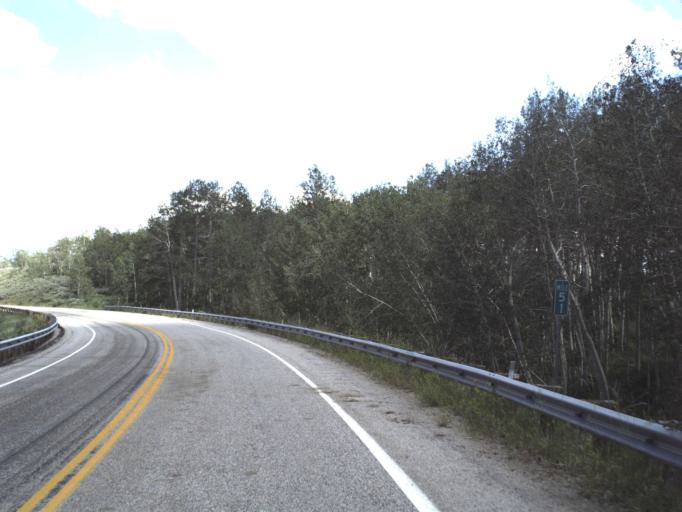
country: US
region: Utah
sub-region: Rich County
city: Randolph
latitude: 41.4741
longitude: -111.4541
